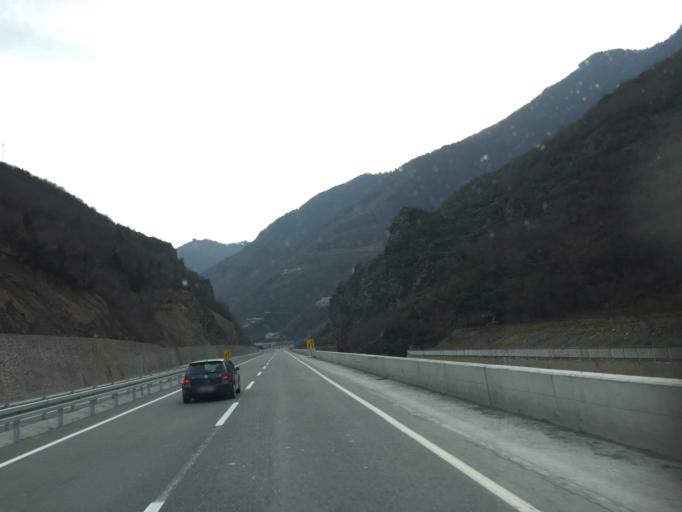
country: TR
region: Trabzon
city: Macka
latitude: 40.7849
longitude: 39.5758
